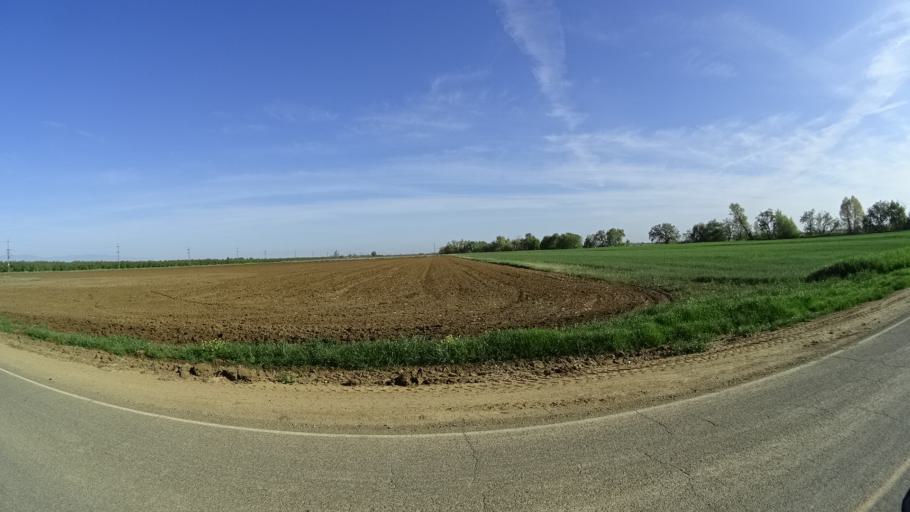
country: US
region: California
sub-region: Glenn County
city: Willows
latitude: 39.5386
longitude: -122.1840
